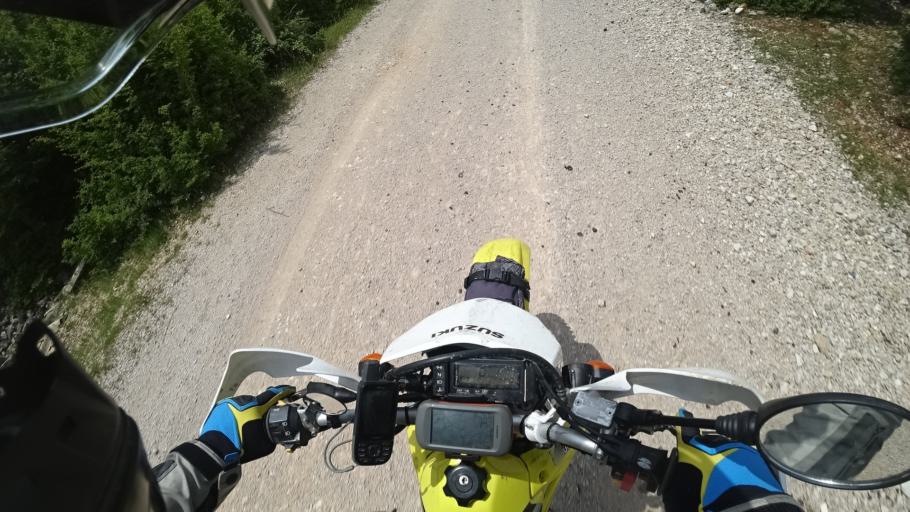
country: HR
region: Sibensko-Kniniska
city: Kistanje
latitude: 44.0624
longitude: 16.0269
